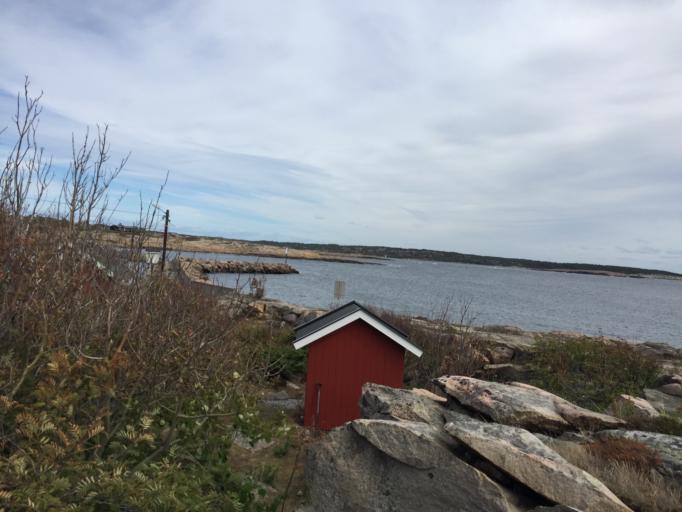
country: NO
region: Ostfold
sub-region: Hvaler
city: Skjaerhalden
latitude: 59.0354
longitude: 10.9478
